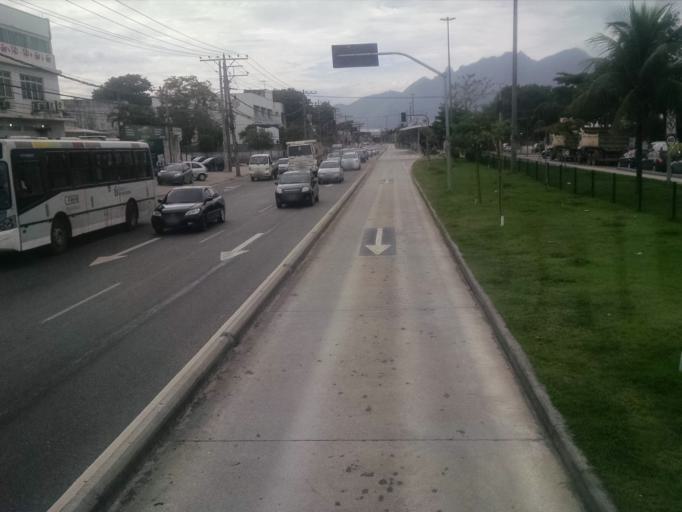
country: BR
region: Rio de Janeiro
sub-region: Nilopolis
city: Nilopolis
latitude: -22.9589
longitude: -43.3849
